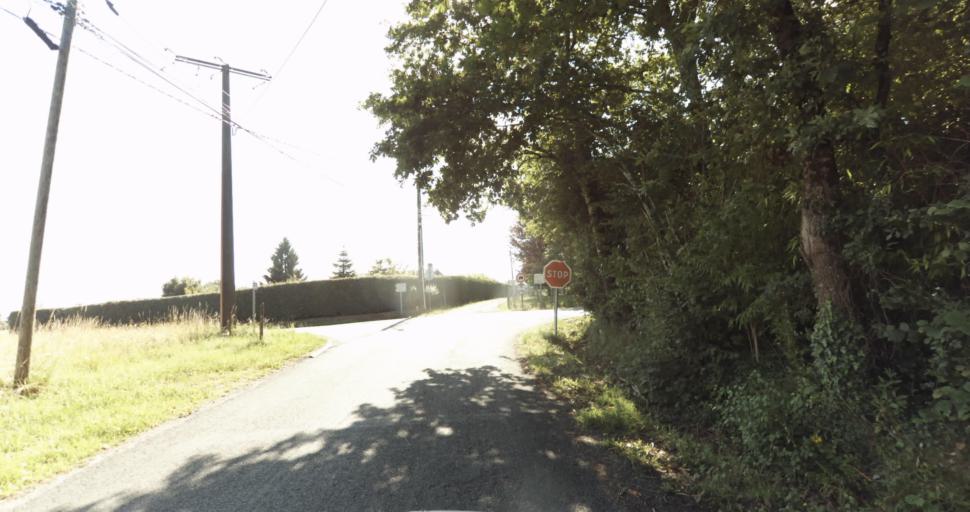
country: FR
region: Aquitaine
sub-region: Departement de la Gironde
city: Bazas
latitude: 44.4250
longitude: -0.2067
